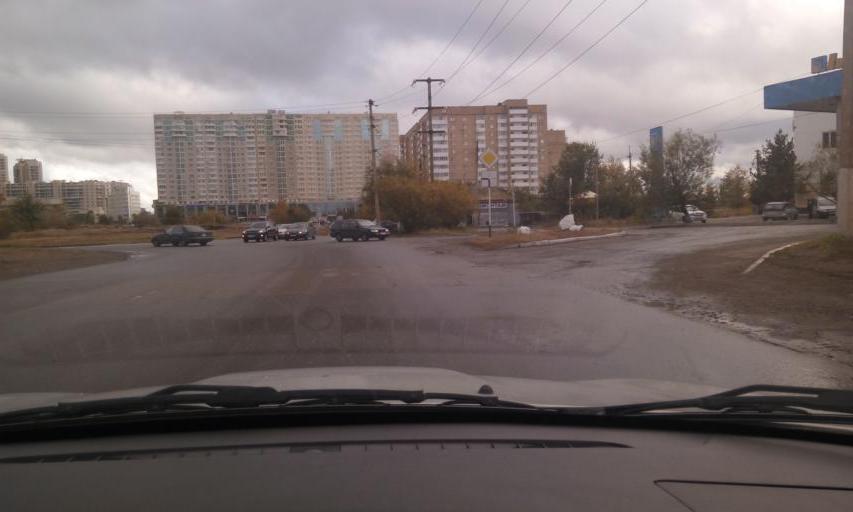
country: KZ
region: Astana Qalasy
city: Astana
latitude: 51.1657
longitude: 71.3998
